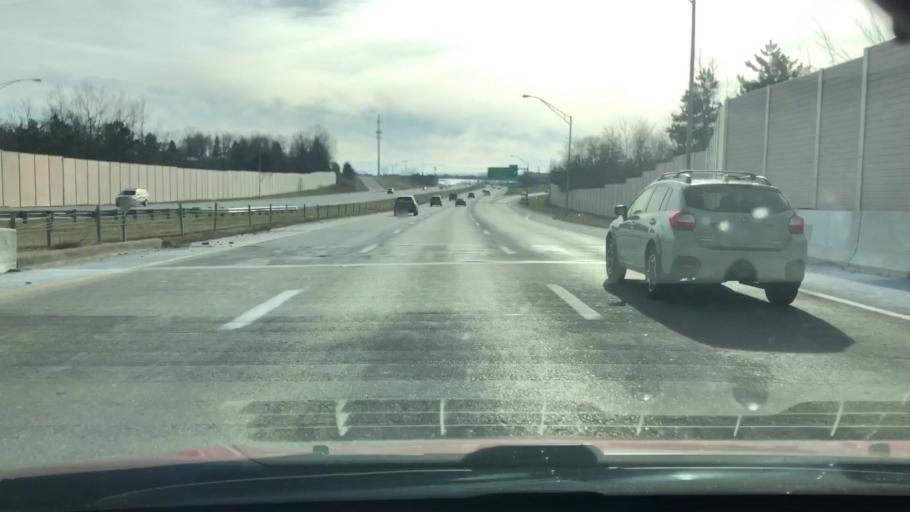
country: US
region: Ohio
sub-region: Greene County
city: Beavercreek
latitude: 39.7017
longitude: -84.0945
